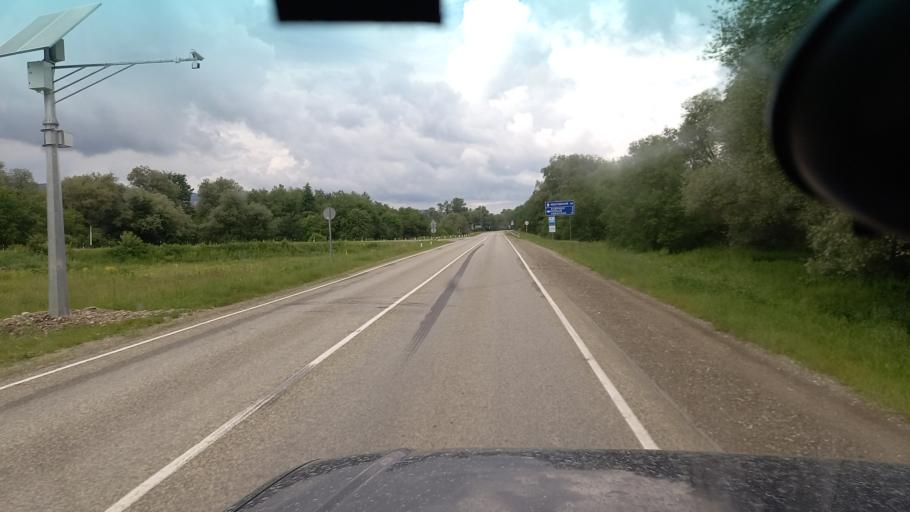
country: RU
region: Krasnodarskiy
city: Psebay
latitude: 44.1008
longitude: 40.8374
